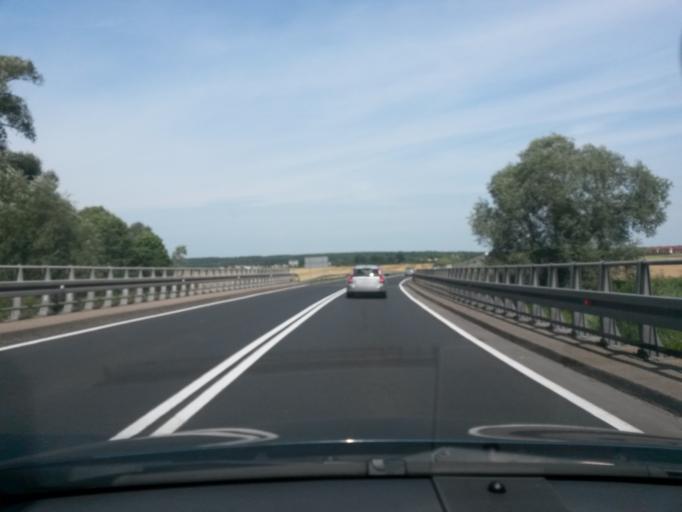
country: PL
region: Lower Silesian Voivodeship
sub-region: Powiat legnicki
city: Prochowice
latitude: 51.2746
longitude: 16.3487
